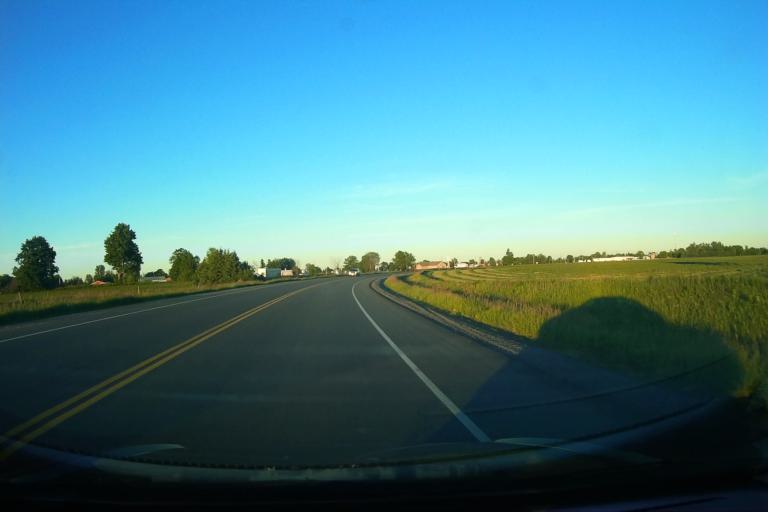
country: CA
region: Ontario
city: Casselman
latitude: 45.0751
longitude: -75.3464
